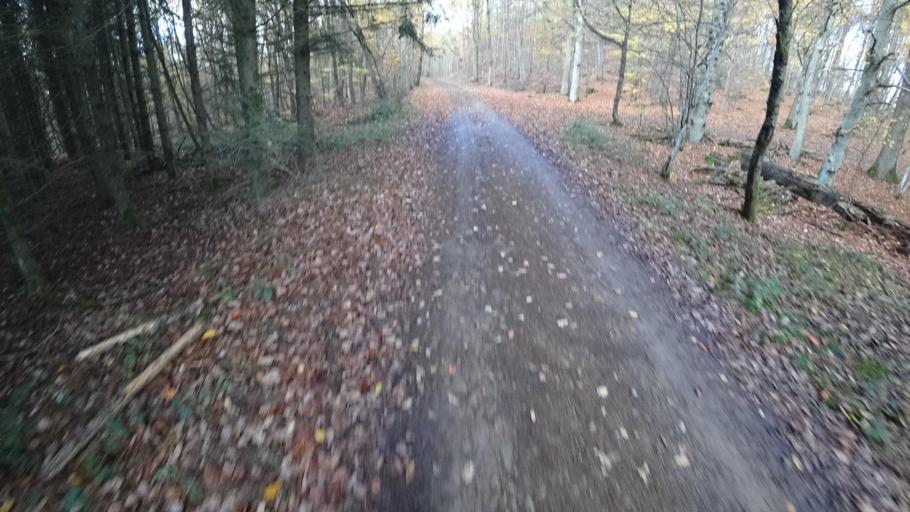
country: DE
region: Rheinland-Pfalz
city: Honningen
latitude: 50.4793
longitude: 6.9372
